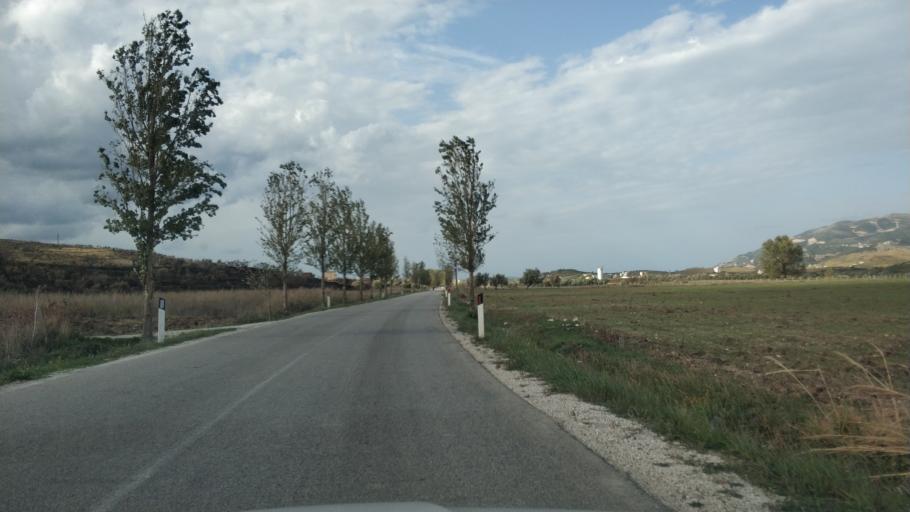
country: AL
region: Vlore
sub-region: Rrethi i Vlores
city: Orikum
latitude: 40.3160
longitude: 19.4847
